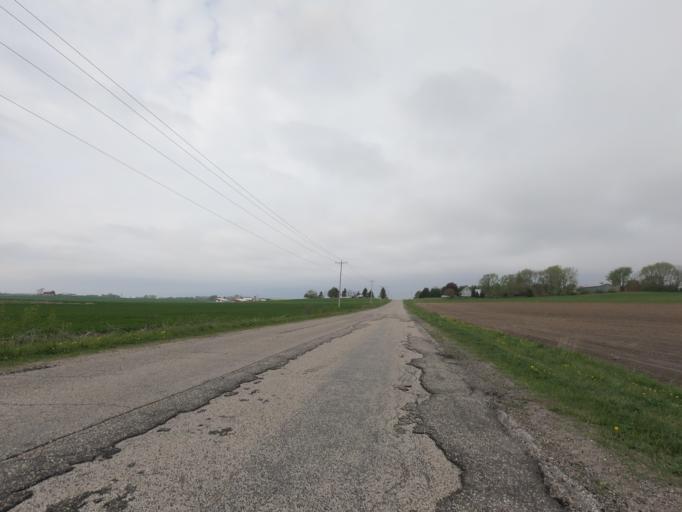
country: US
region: Wisconsin
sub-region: Jefferson County
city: Jefferson
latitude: 43.0319
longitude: -88.7784
